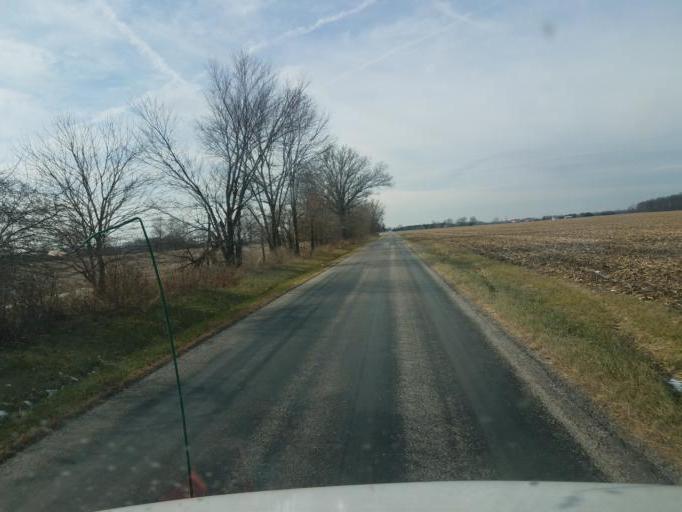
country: US
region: Ohio
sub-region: Delaware County
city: Ashley
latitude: 40.3848
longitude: -82.9508
